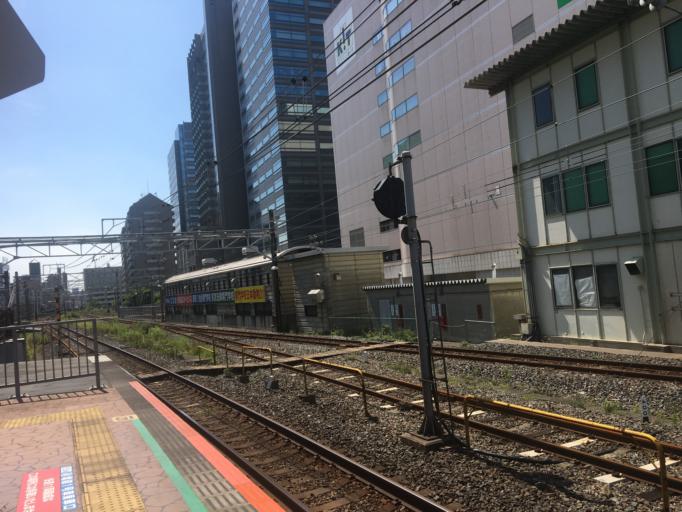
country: JP
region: Tokyo
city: Urayasu
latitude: 35.6969
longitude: 139.8131
